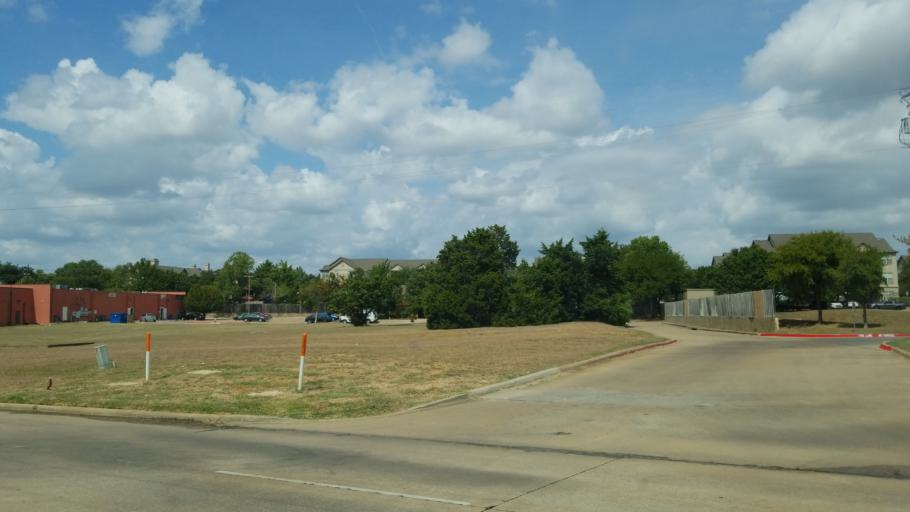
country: US
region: Texas
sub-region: Tarrant County
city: Euless
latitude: 32.8699
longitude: -97.0723
